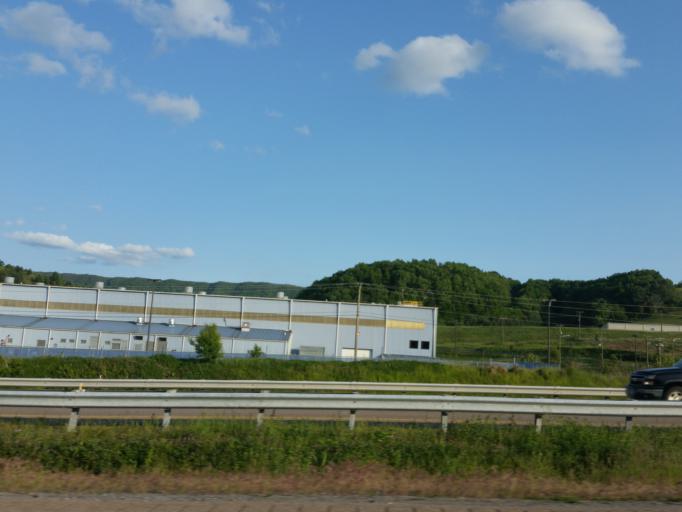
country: US
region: Virginia
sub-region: Russell County
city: Lebanon
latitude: 36.9019
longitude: -82.0491
